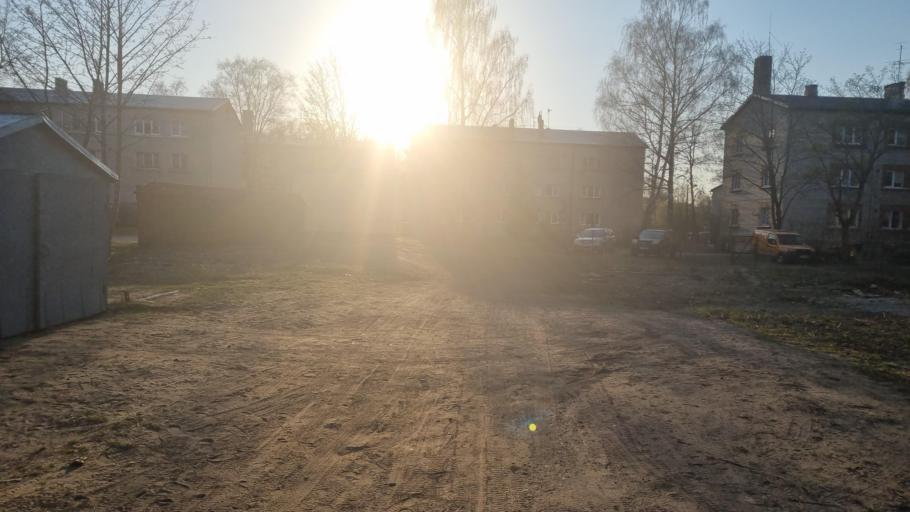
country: LV
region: Kekava
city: Balozi
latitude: 56.9105
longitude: 24.1167
